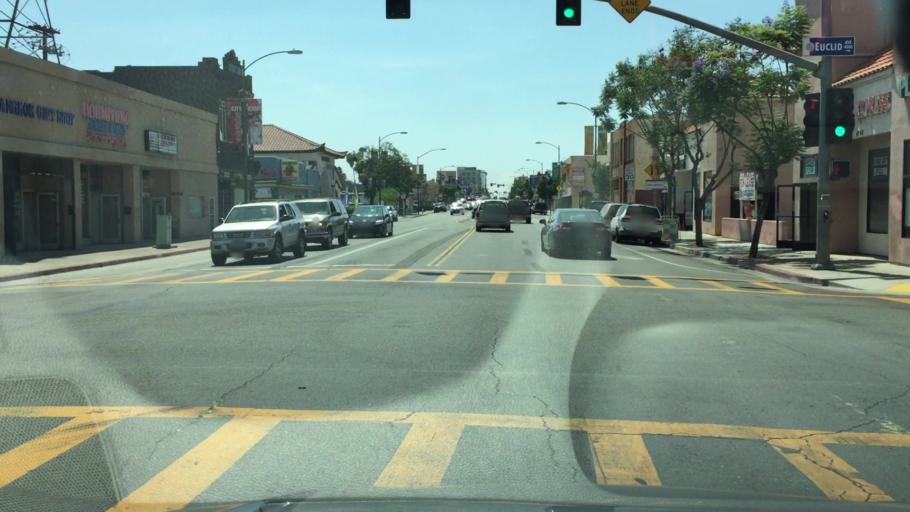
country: US
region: California
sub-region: San Diego County
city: Lemon Grove
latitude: 32.7496
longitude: -117.0922
